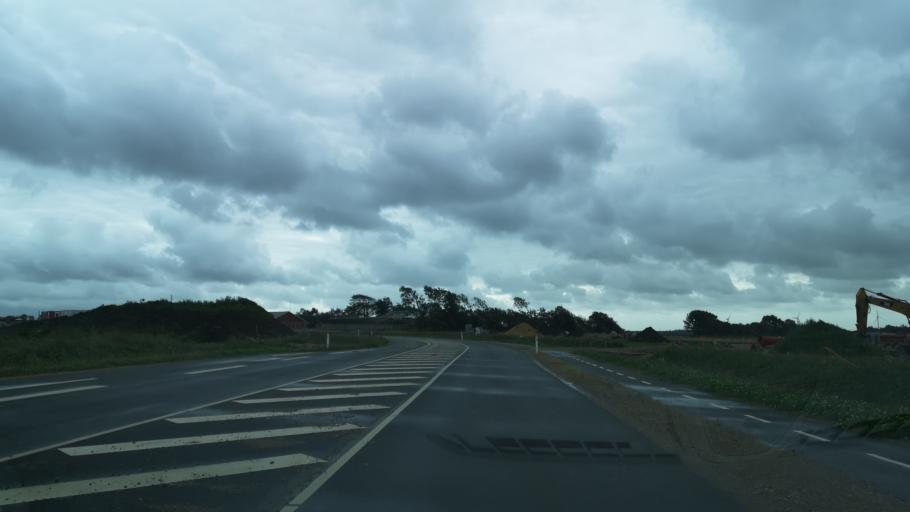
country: DK
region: Central Jutland
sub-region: Ringkobing-Skjern Kommune
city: Videbaek
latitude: 56.0476
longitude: 8.6646
